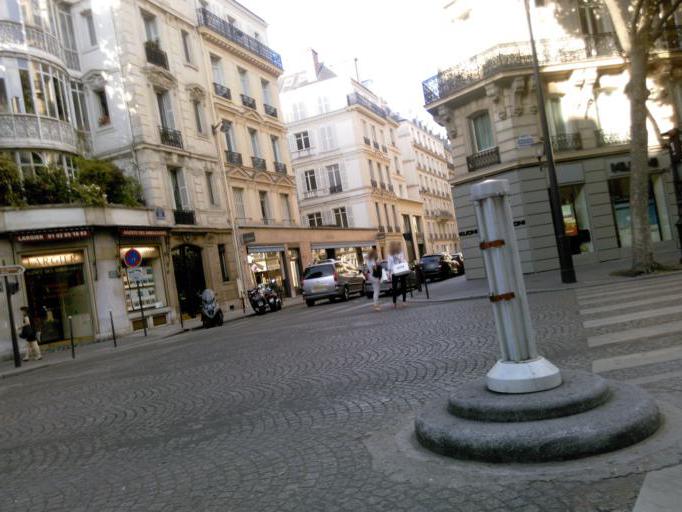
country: FR
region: Ile-de-France
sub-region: Departement des Hauts-de-Seine
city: Clichy
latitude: 48.8733
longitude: 2.3209
